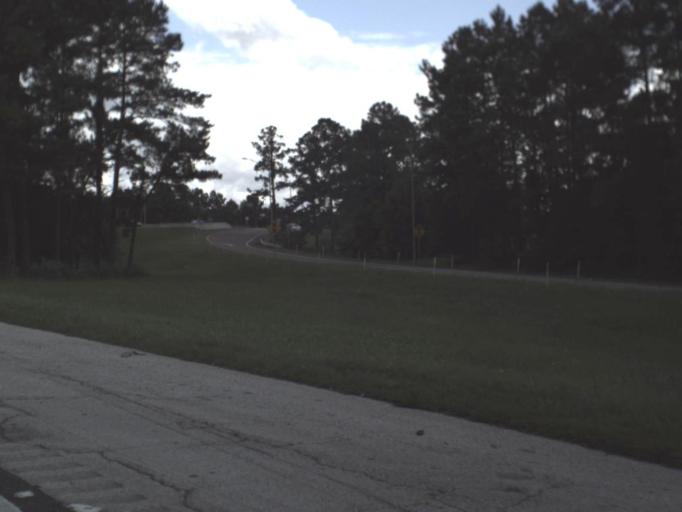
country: US
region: Florida
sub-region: Alachua County
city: Alachua
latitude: 29.6914
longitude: -82.4492
